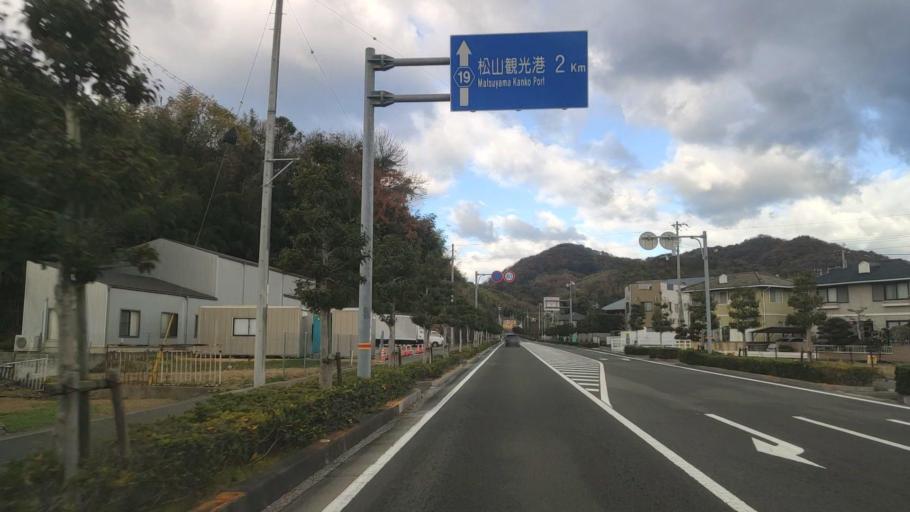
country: JP
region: Ehime
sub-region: Shikoku-chuo Shi
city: Matsuyama
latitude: 33.8722
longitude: 132.7192
